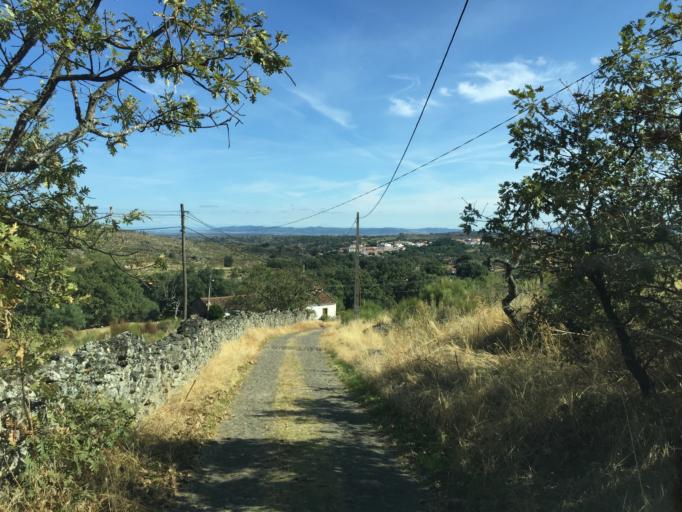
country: PT
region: Portalegre
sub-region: Marvao
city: Marvao
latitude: 39.4019
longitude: -7.3649
